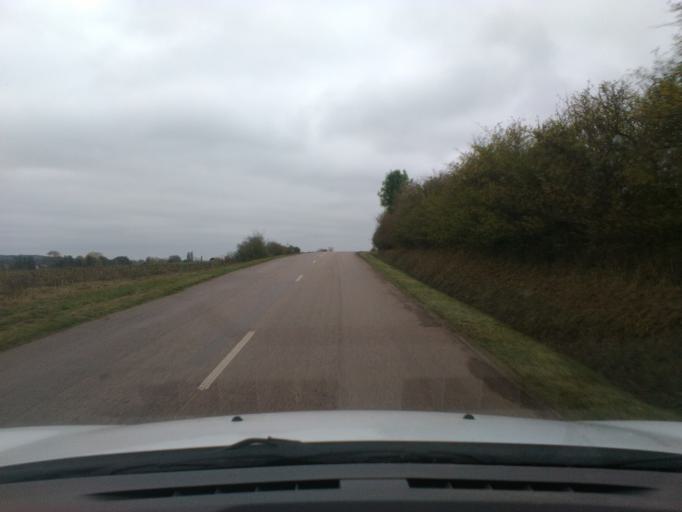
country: FR
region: Lorraine
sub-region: Departement des Vosges
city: Aydoilles
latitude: 48.2533
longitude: 6.5783
